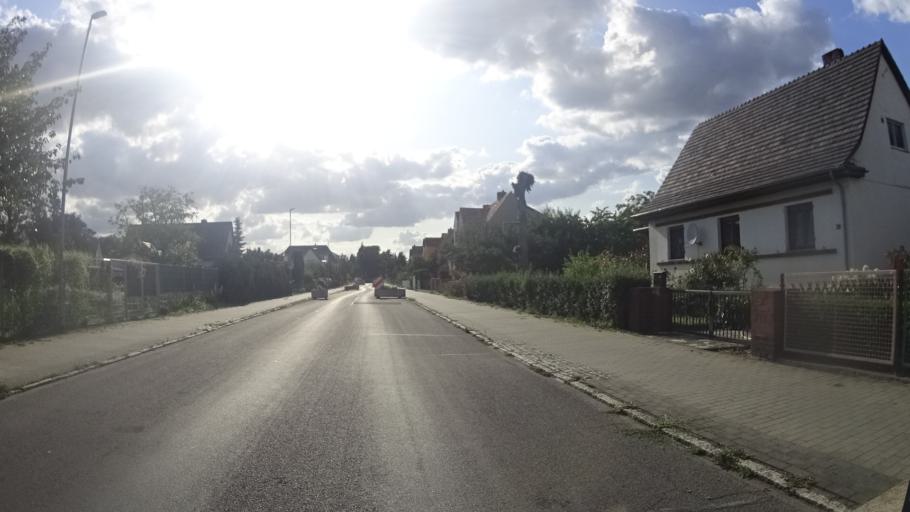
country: DE
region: Brandenburg
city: Rathenow
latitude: 52.5933
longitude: 12.3411
